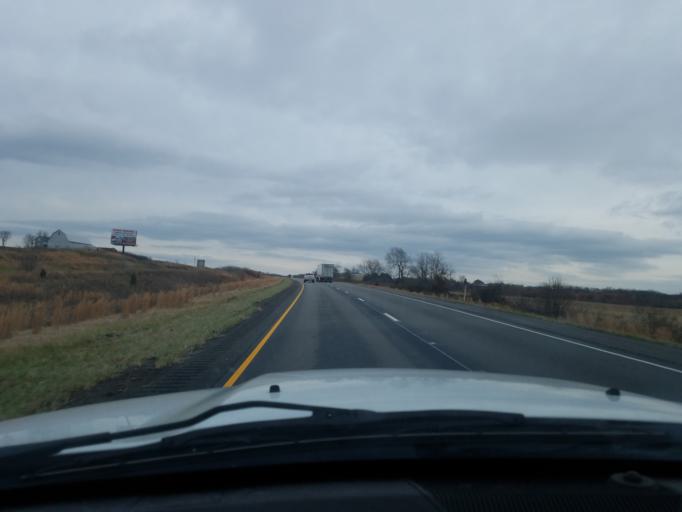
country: US
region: Indiana
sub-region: Dubois County
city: Ferdinand
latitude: 38.2021
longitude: -86.8311
